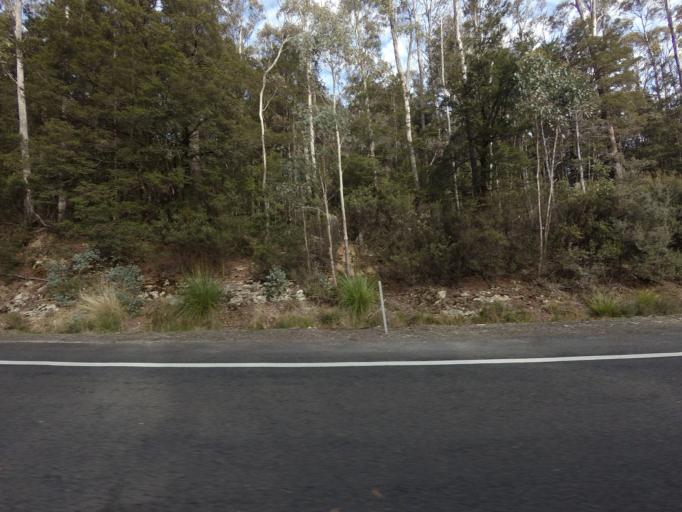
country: AU
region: Tasmania
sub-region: Meander Valley
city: Deloraine
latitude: -41.7001
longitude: 146.7237
